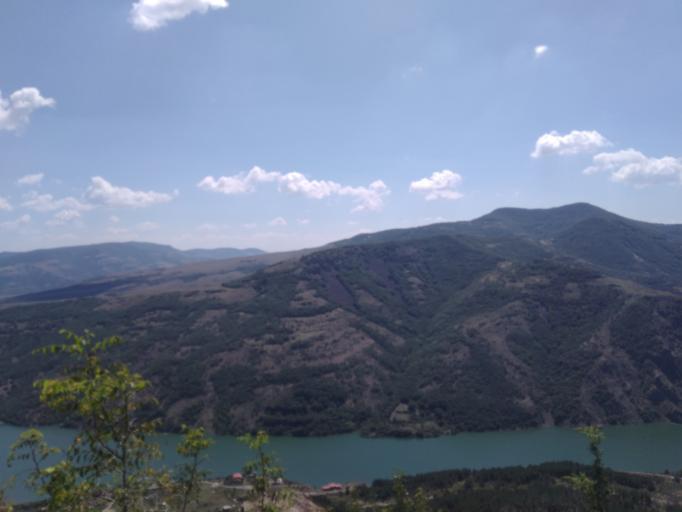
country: BG
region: Kurdzhali
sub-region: Obshtina Kurdzhali
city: Kurdzhali
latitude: 41.6226
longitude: 25.4629
